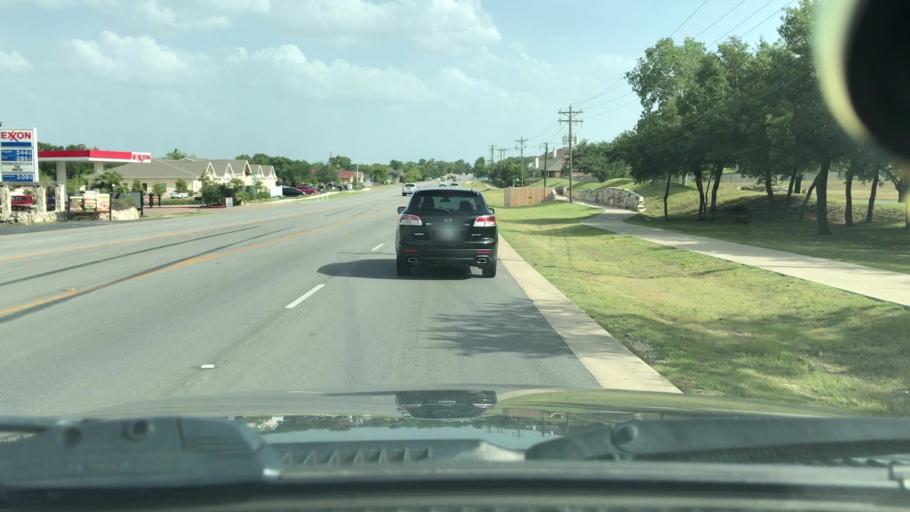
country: US
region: Texas
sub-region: Williamson County
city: Leander
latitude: 30.5496
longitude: -97.8535
